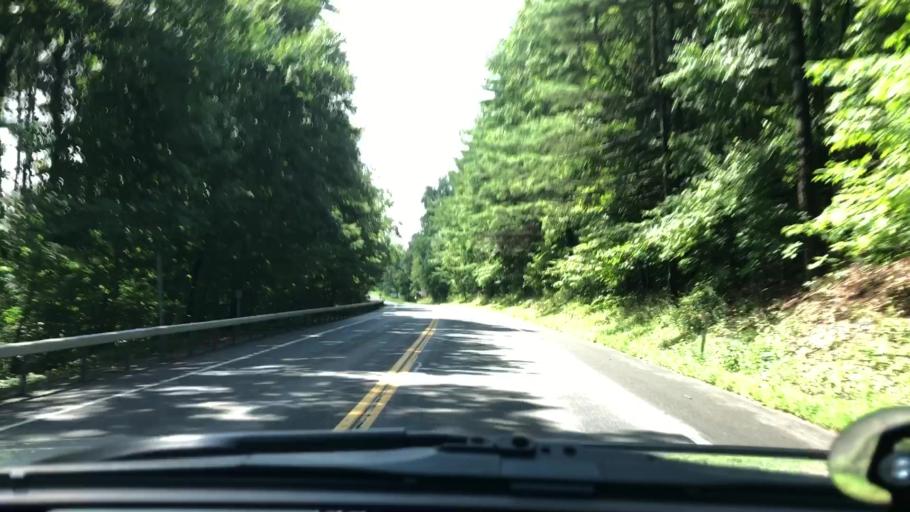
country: US
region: New York
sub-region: Greene County
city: Palenville
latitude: 42.1983
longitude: -73.9860
